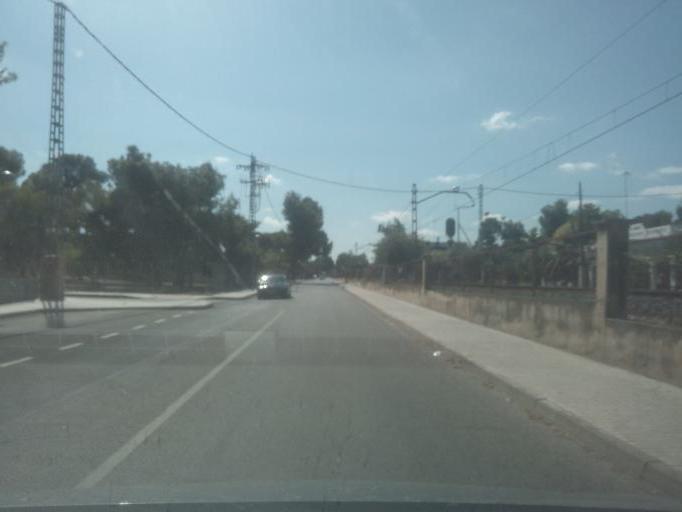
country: ES
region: Valencia
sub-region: Provincia de Valencia
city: Manises
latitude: 39.5320
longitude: -0.4909
